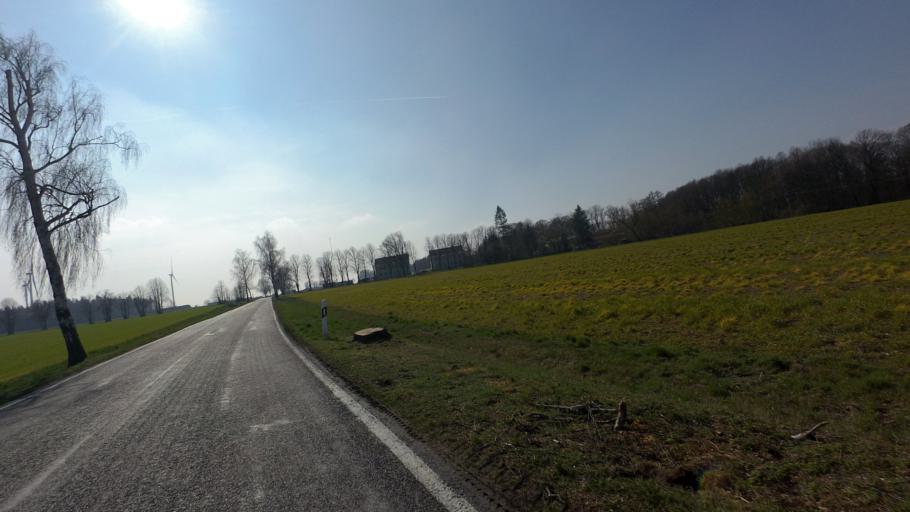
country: DE
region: Brandenburg
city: Dahme
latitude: 51.9033
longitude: 13.4960
